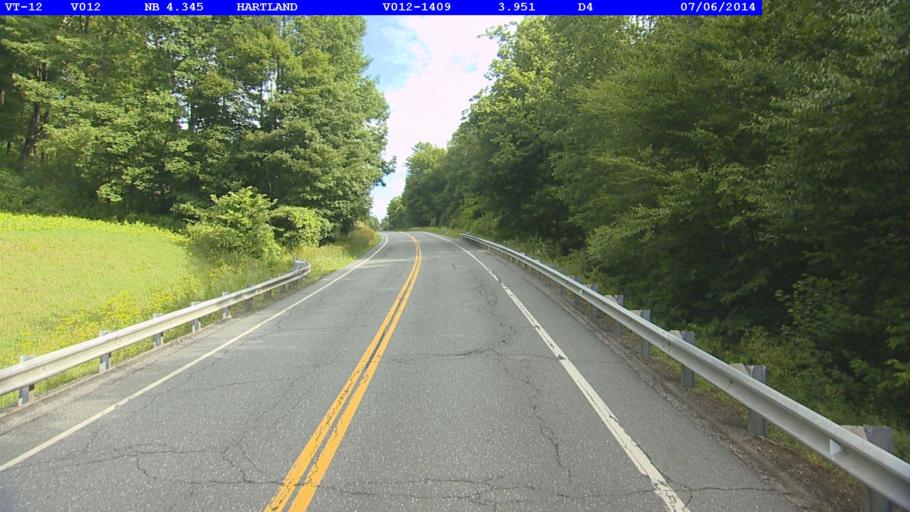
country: US
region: Vermont
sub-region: Windsor County
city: Woodstock
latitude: 43.5756
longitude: -72.4437
